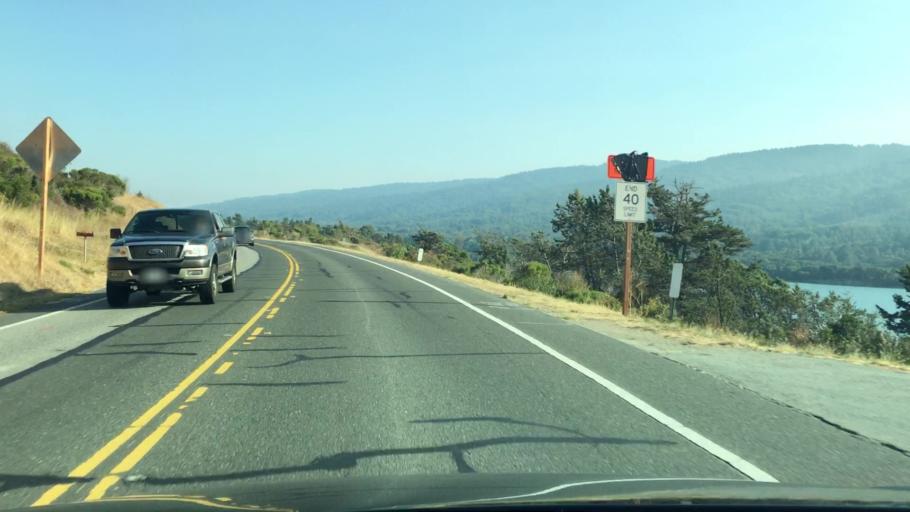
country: US
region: California
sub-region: San Mateo County
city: Highlands-Baywood Park
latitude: 37.4952
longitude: -122.3271
